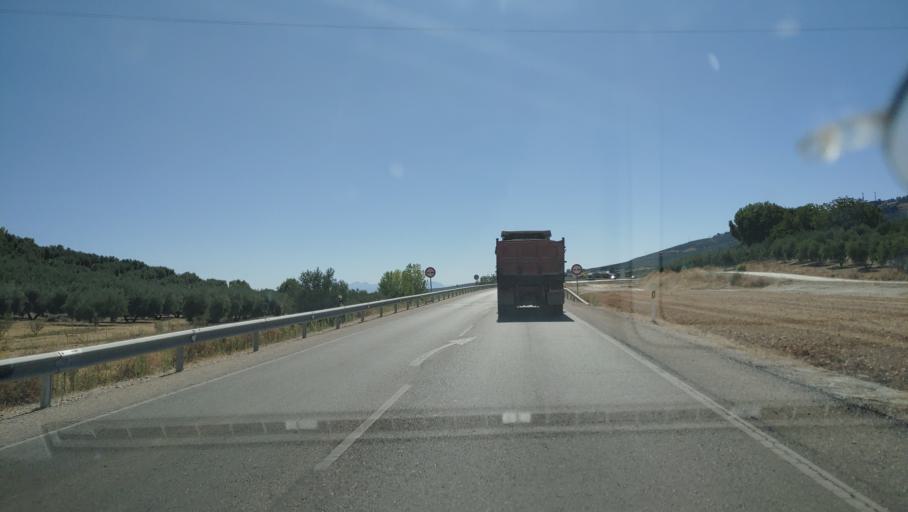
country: ES
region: Andalusia
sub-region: Provincia de Jaen
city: Villanueva del Arzobispo
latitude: 38.1564
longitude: -3.0028
